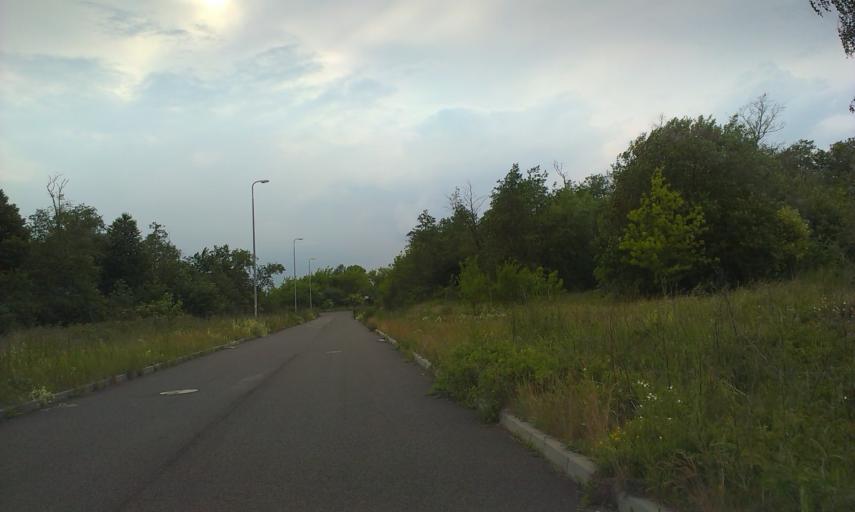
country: PL
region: West Pomeranian Voivodeship
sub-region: Powiat szczecinecki
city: Szczecinek
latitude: 53.7354
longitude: 16.6720
